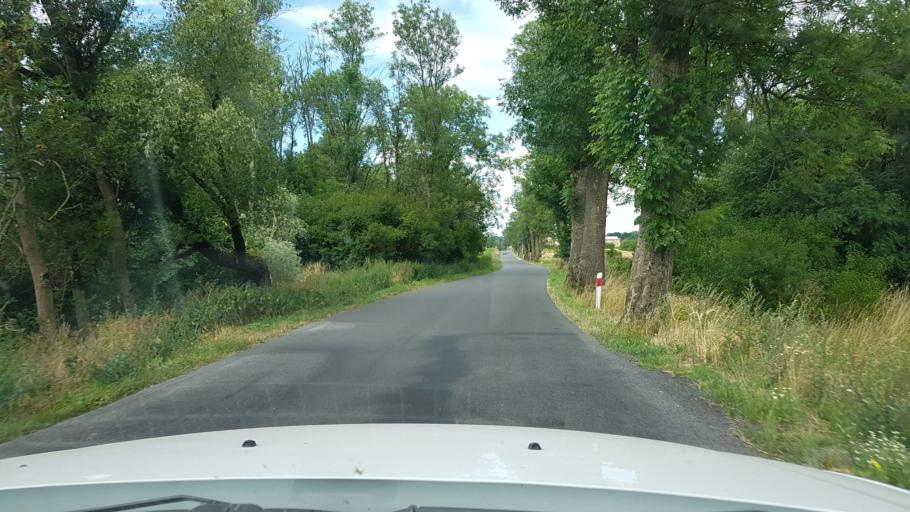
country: PL
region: West Pomeranian Voivodeship
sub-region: Powiat drawski
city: Kalisz Pomorski
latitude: 53.3275
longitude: 15.9270
